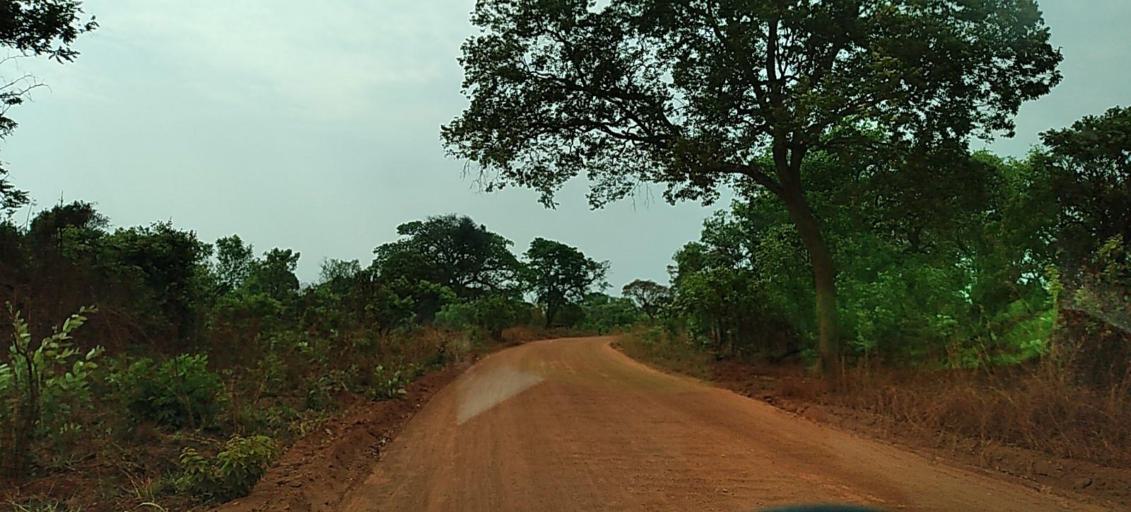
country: ZM
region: North-Western
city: Solwezi
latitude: -12.2178
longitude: 26.5085
